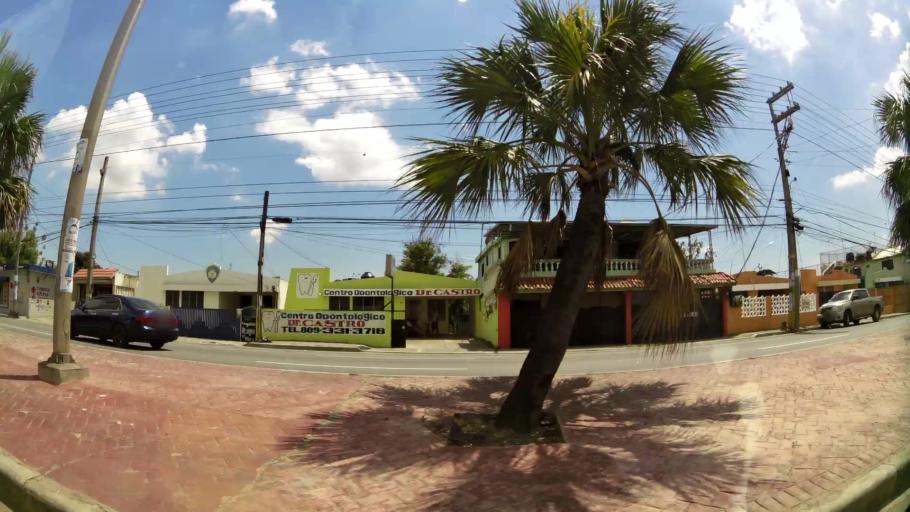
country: DO
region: Nacional
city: Ensanche Luperon
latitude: 18.5473
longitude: -69.9084
